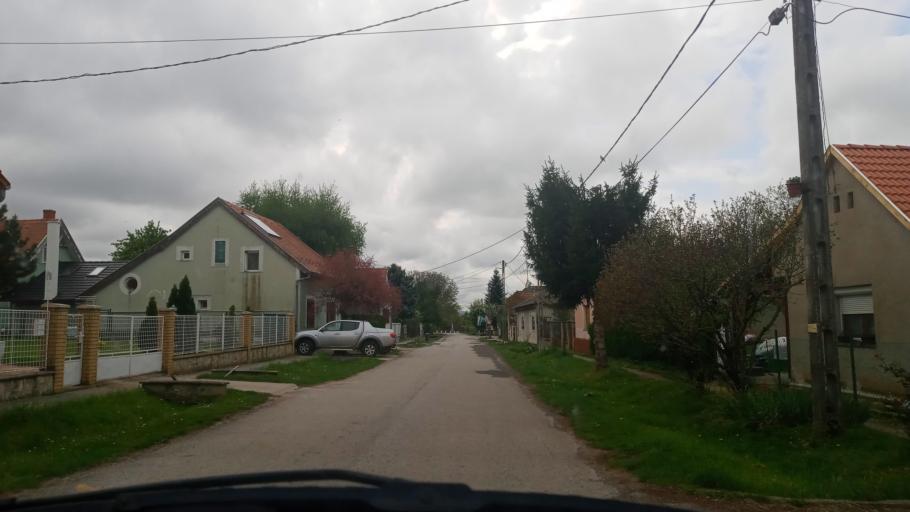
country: HU
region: Baranya
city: Kozarmisleny
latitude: 45.9987
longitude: 18.3755
